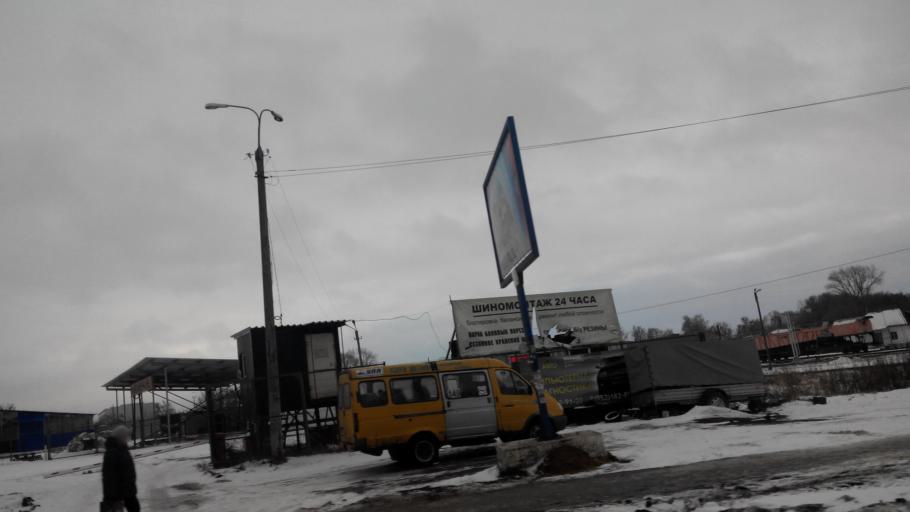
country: RU
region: Tula
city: Uzlovaya
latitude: 53.9729
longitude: 38.1789
